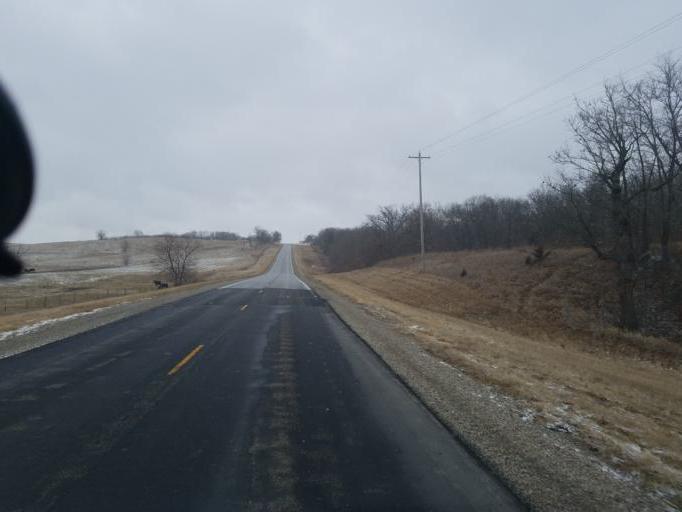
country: US
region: Missouri
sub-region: Putnam County
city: Unionville
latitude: 40.5294
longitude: -93.0159
